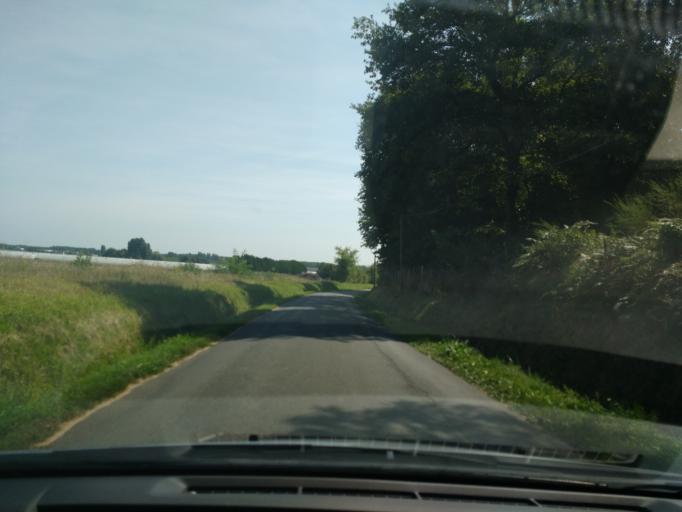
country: FR
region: Pays de la Loire
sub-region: Departement de Maine-et-Loire
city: Maze
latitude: 47.4733
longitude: -0.2670
